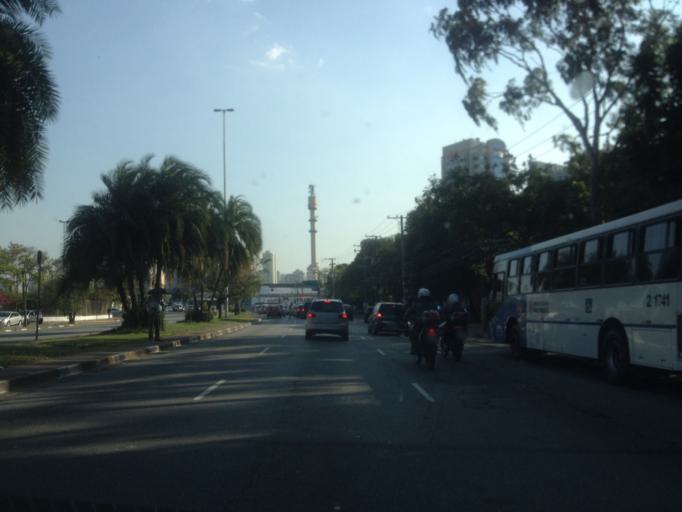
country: BR
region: Sao Paulo
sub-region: Sao Paulo
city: Sao Paulo
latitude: -23.5214
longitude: -46.6585
